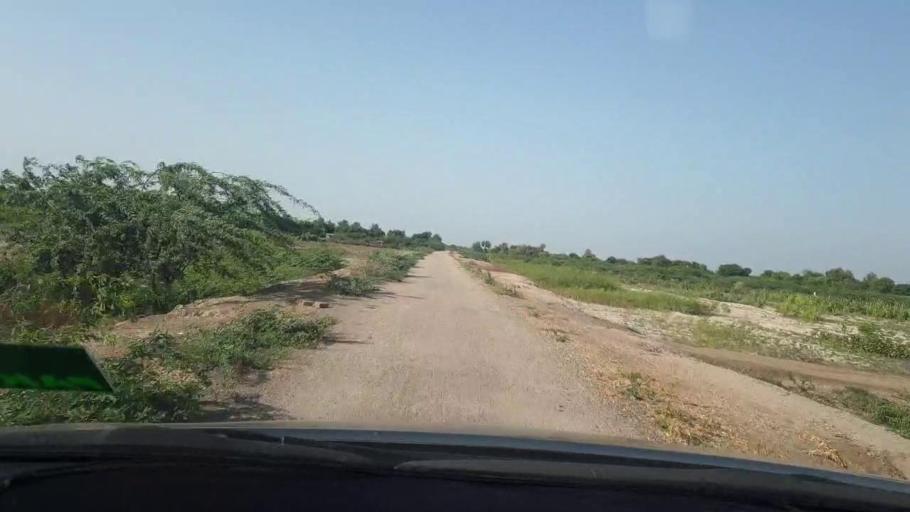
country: PK
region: Sindh
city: Naukot
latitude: 24.8645
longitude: 69.3181
